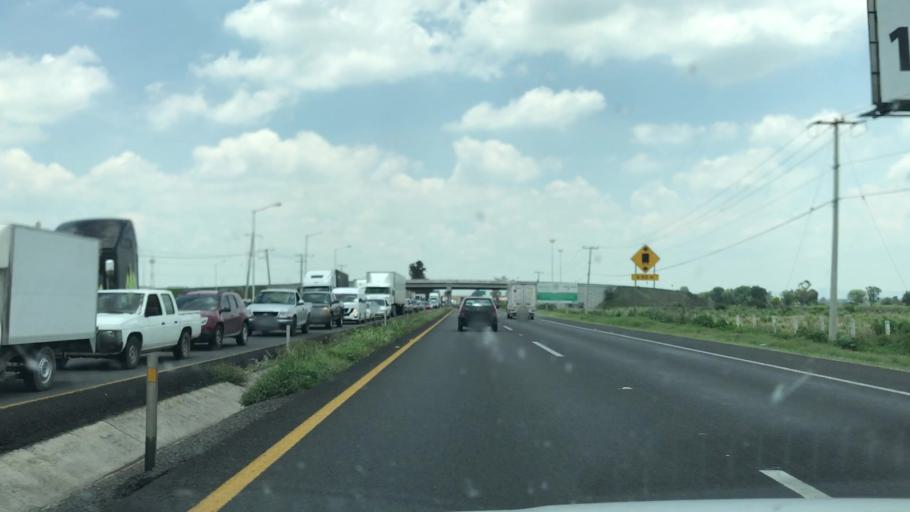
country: MX
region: Guanajuato
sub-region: Irapuato
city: Colonia Morelos de Guadalupe de Rivera
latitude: 20.5911
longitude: -101.4249
